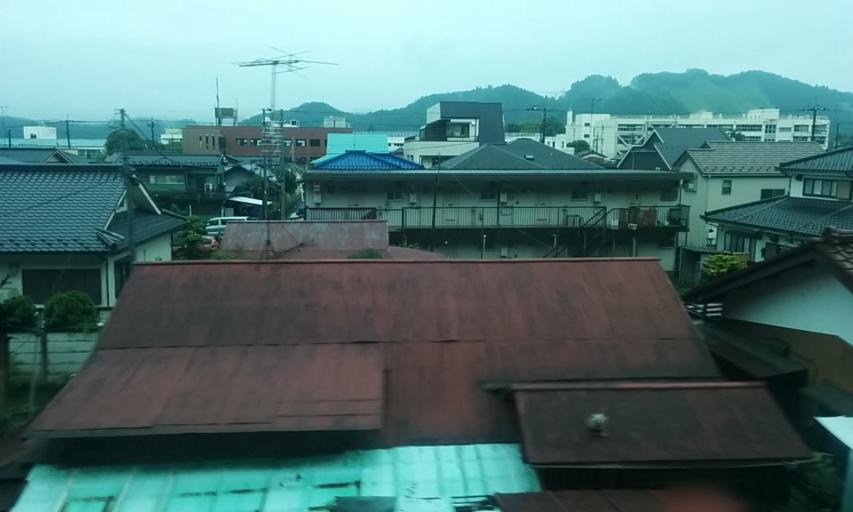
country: JP
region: Tokyo
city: Ome
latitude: 35.7916
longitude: 139.2465
